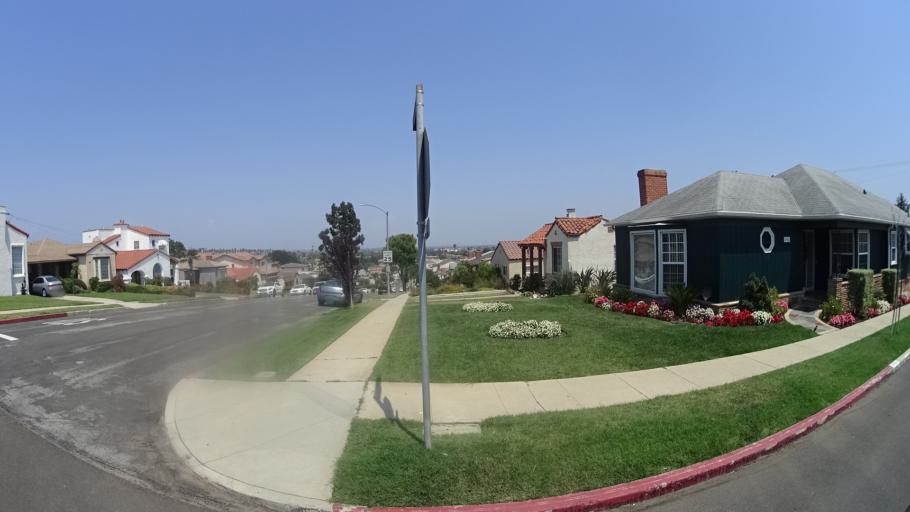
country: US
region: California
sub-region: Los Angeles County
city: View Park-Windsor Hills
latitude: 33.9860
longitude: -118.3500
